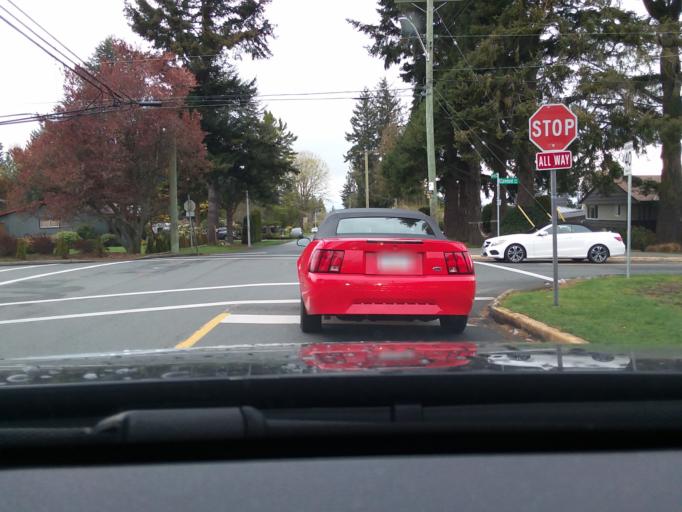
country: CA
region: British Columbia
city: Victoria
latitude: 48.5178
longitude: -123.3741
